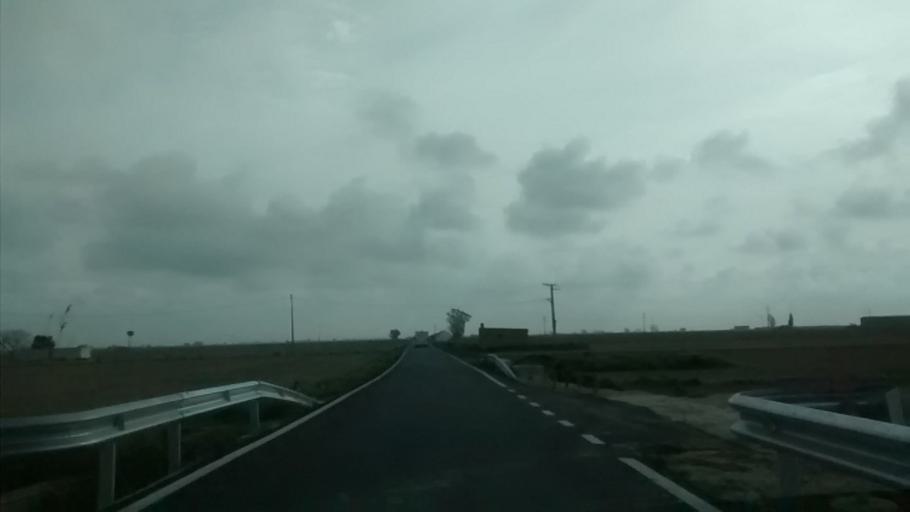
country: ES
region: Catalonia
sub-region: Provincia de Tarragona
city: Deltebre
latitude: 40.6730
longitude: 0.6538
